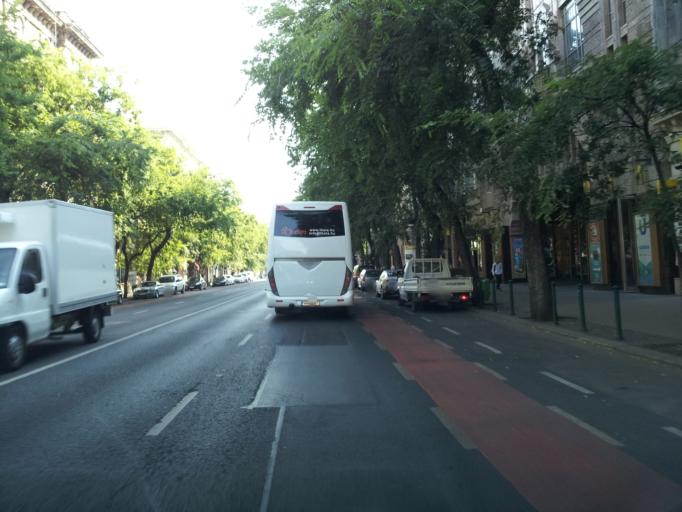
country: HU
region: Budapest
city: Budapest VI. keruelet
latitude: 47.5037
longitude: 19.0612
